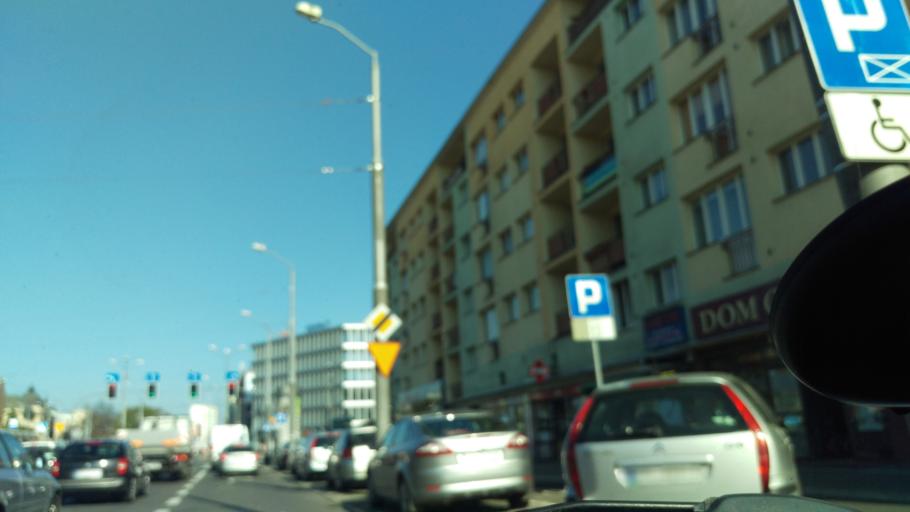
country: PL
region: West Pomeranian Voivodeship
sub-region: Szczecin
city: Szczecin
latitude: 53.4239
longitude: 14.5509
